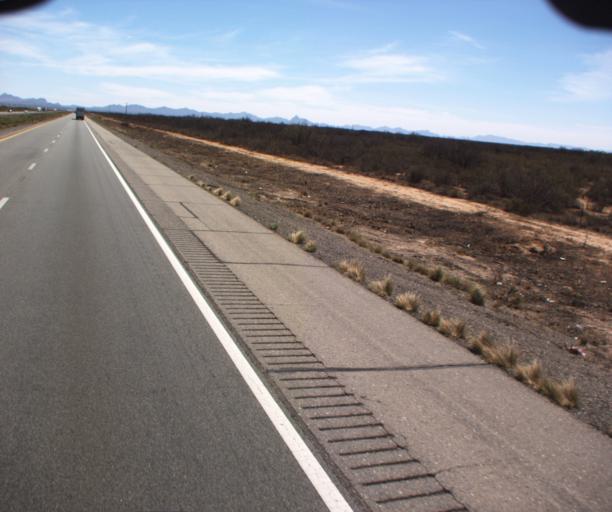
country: US
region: Arizona
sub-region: Cochise County
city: Willcox
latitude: 32.2829
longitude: -109.2919
